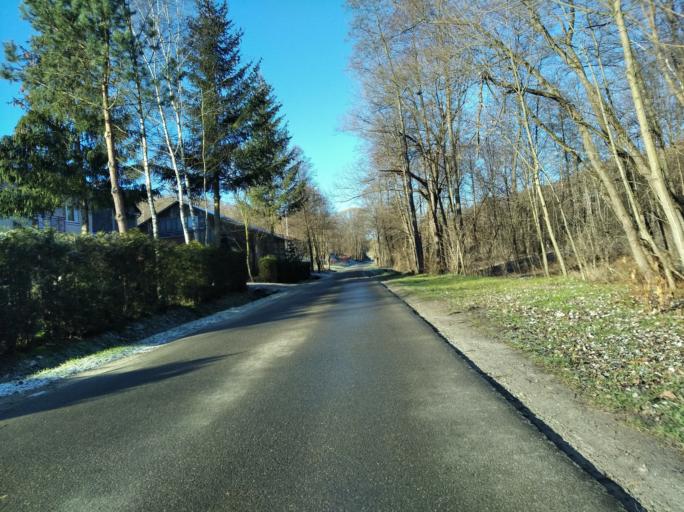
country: PL
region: Subcarpathian Voivodeship
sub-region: Powiat strzyzowski
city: Czudec
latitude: 49.9520
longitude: 21.7742
